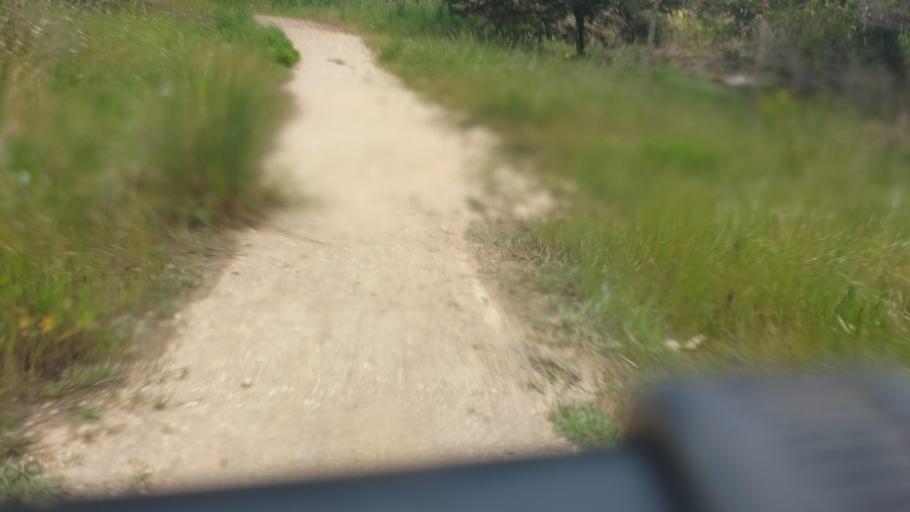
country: AU
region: Victoria
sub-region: Mount Alexander
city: Castlemaine
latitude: -37.0734
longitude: 144.2029
